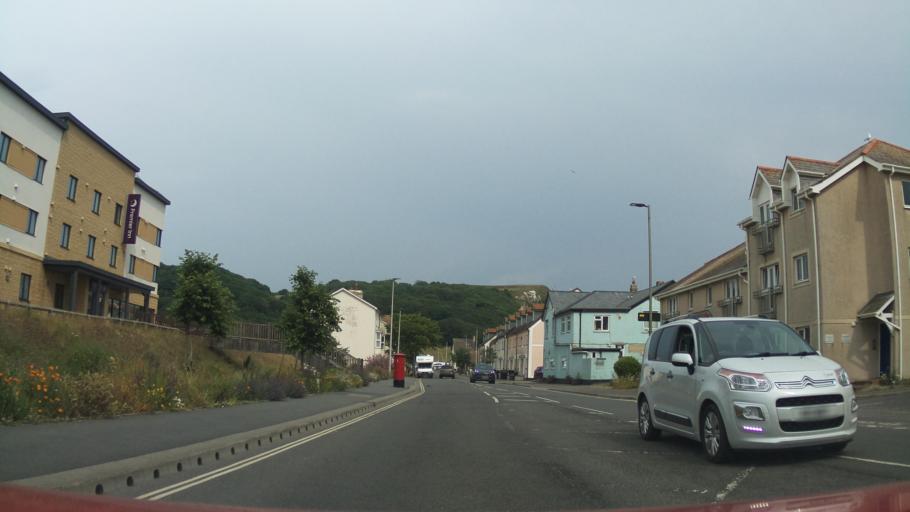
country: GB
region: England
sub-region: Devon
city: Colyton
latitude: 50.7044
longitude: -3.0648
